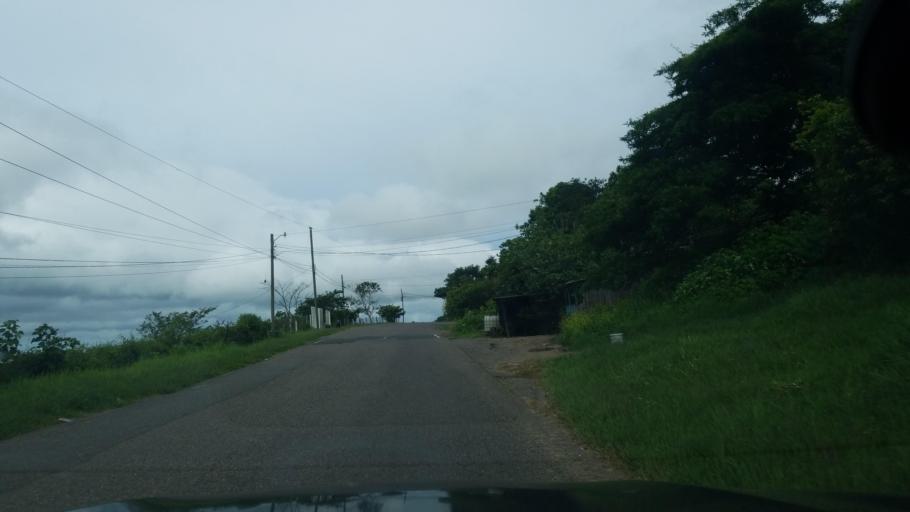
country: HN
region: Choluteca
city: Corpus
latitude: 13.3667
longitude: -86.9220
